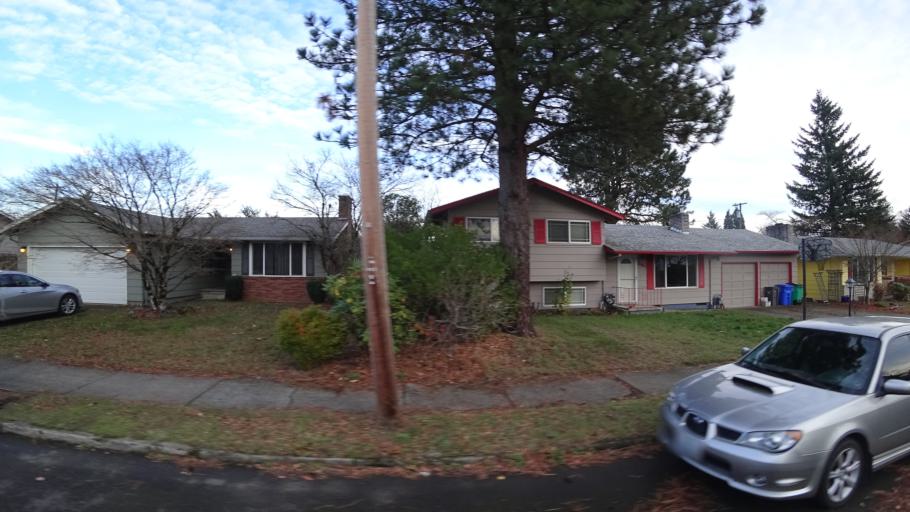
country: US
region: Oregon
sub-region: Multnomah County
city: Lents
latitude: 45.5164
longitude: -122.5172
